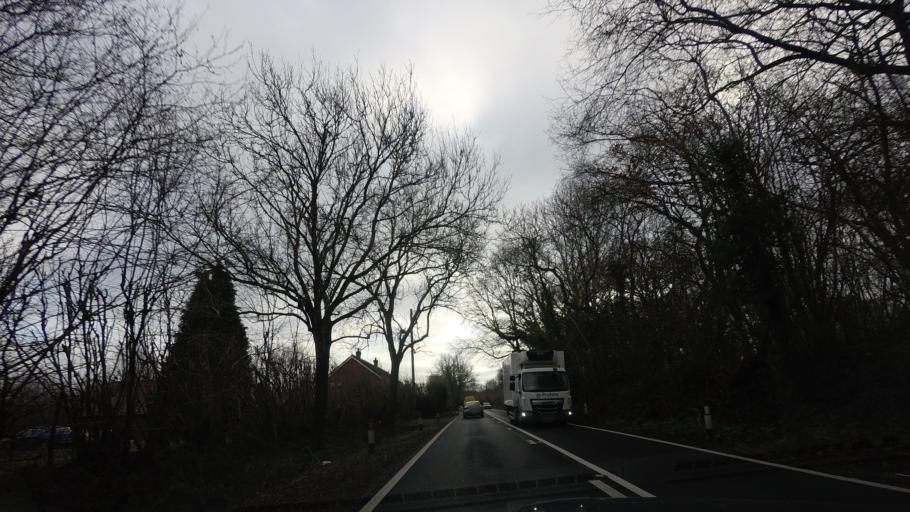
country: GB
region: England
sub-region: East Sussex
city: Wadhurst
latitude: 51.0752
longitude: 0.4206
